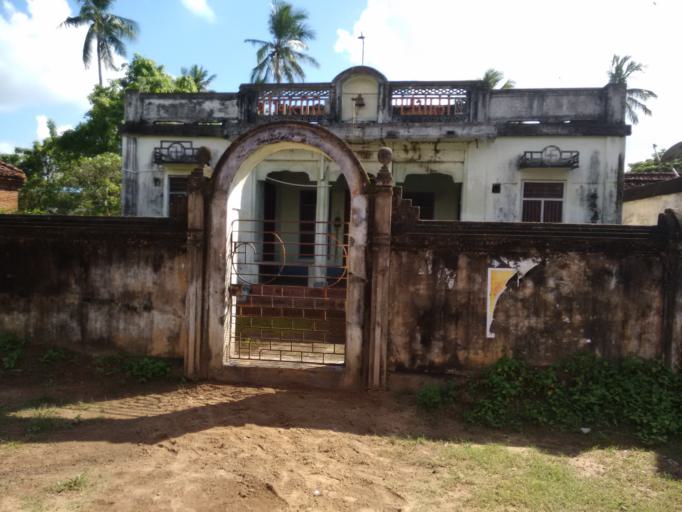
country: IN
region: Tamil Nadu
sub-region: Thiruvarur
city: Koradachcheri
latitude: 10.8505
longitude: 79.5137
